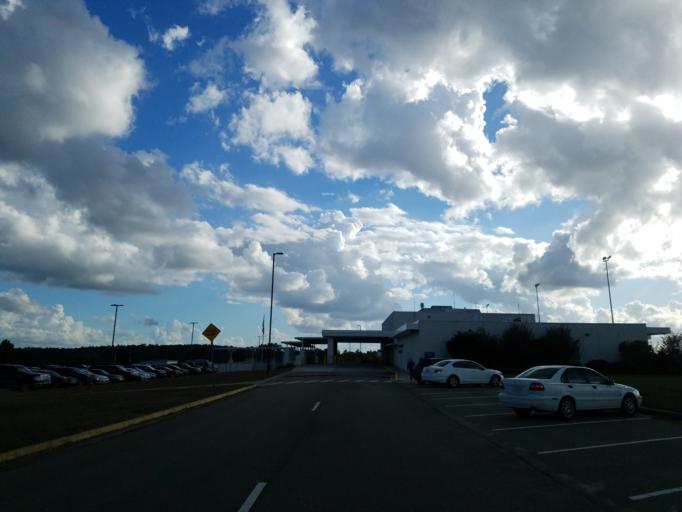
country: US
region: Mississippi
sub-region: Forrest County
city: Rawls Springs
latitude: 31.4677
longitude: -89.3333
